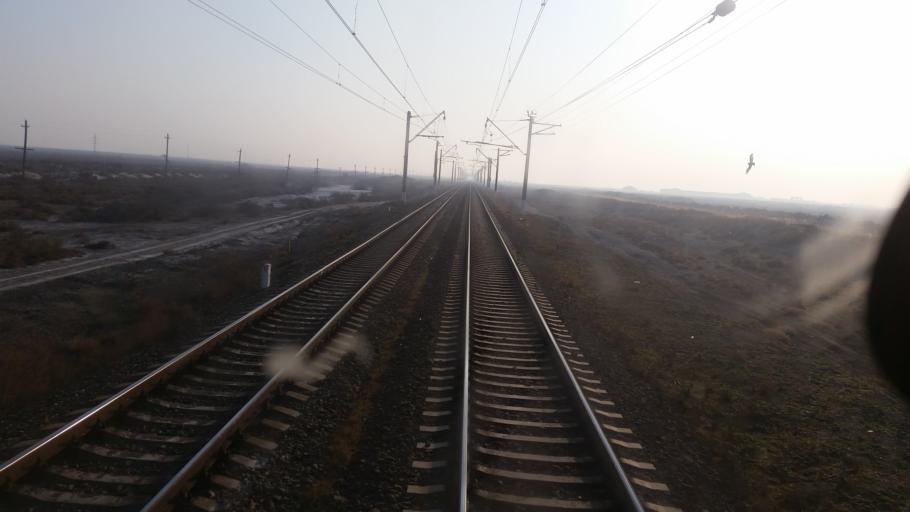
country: AZ
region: Yevlax City
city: Yevlakh
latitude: 40.5940
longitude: 47.2721
